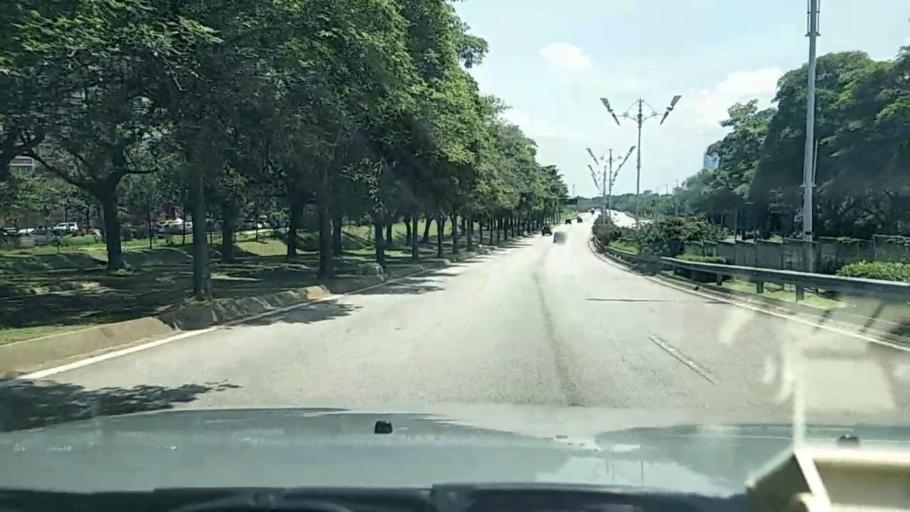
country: MY
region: Putrajaya
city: Putrajaya
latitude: 2.9464
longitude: 101.6769
